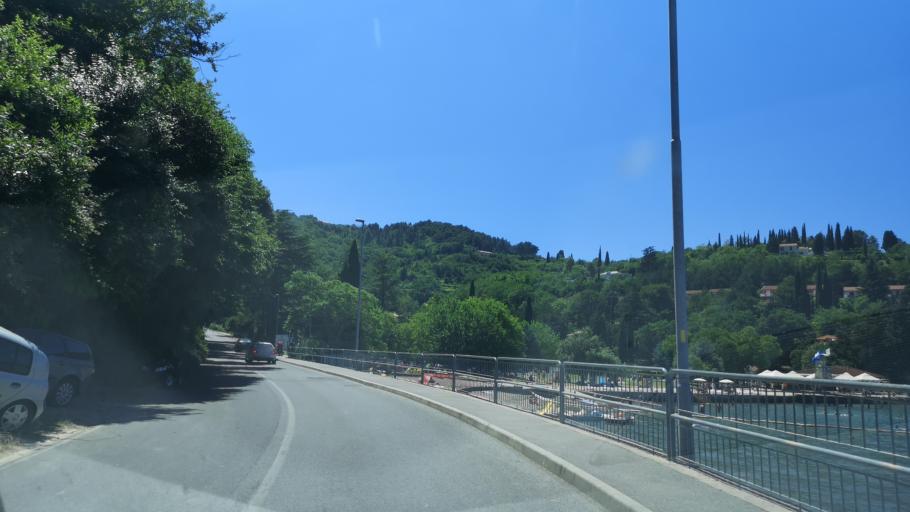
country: SI
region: Piran-Pirano
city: Portoroz
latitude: 45.5258
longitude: 13.6007
